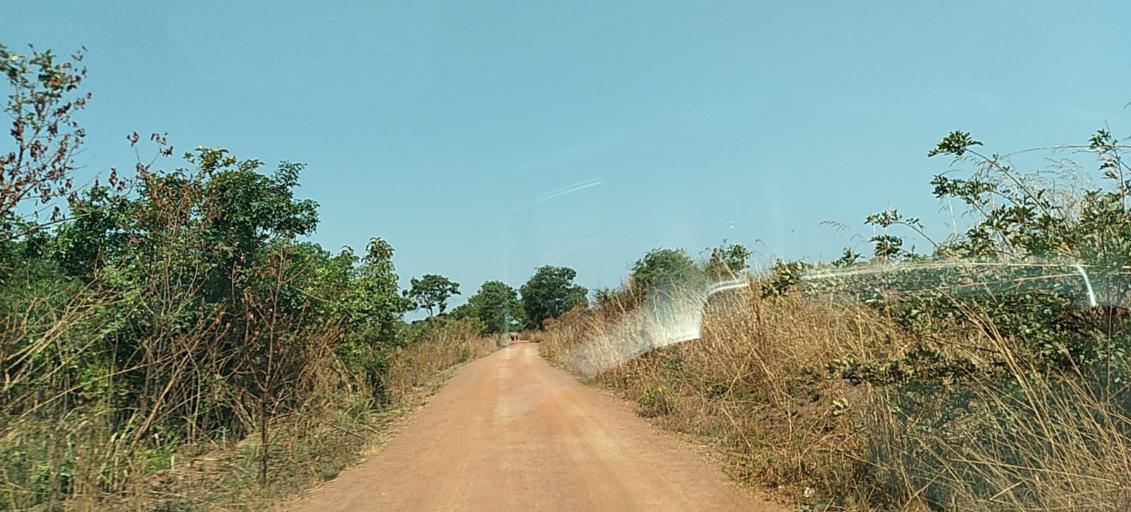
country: ZM
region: Copperbelt
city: Chingola
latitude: -12.5445
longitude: 27.7480
